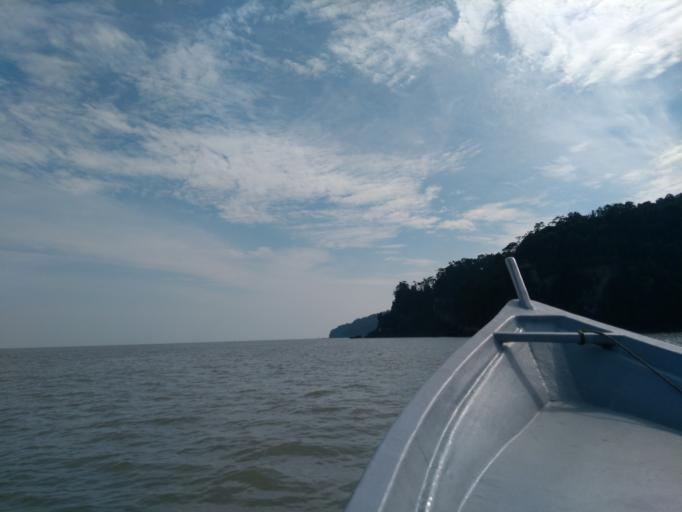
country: MY
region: Sarawak
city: Kuching
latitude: 1.7134
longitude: 110.4381
